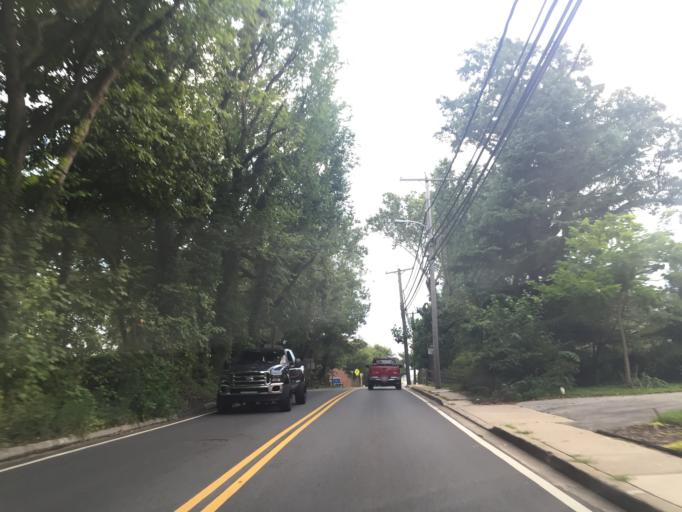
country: US
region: Maryland
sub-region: Anne Arundel County
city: Linthicum
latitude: 39.2043
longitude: -76.6530
